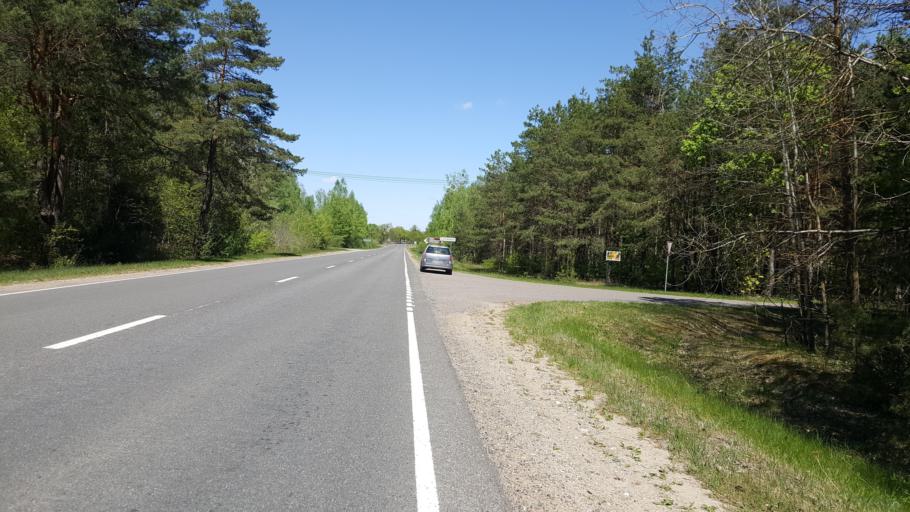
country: BY
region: Brest
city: Kamyanyuki
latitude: 52.5510
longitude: 23.7939
